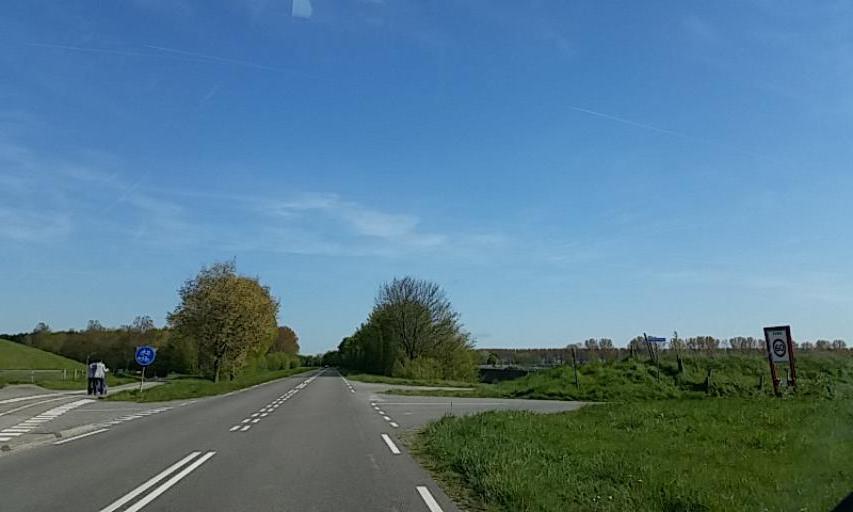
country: NL
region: Zeeland
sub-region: Gemeente Vlissingen
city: Vlissingen
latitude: 51.3875
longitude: 3.5839
